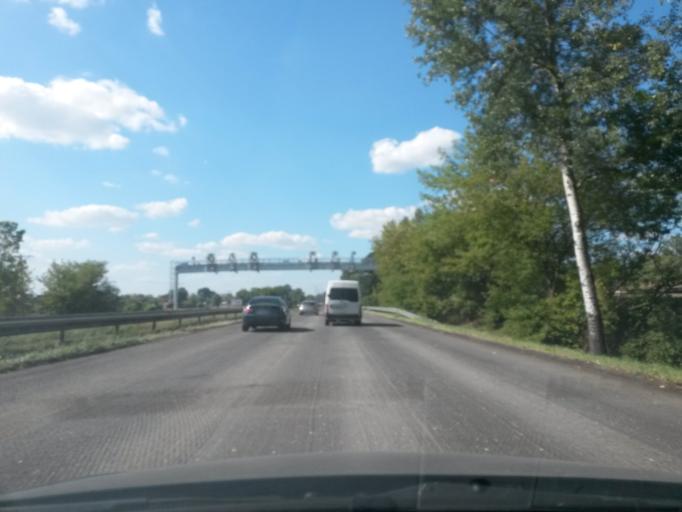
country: PL
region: Masovian Voivodeship
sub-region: Powiat nowodworski
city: Nowy Dwor Mazowiecki
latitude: 52.4055
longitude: 20.7048
